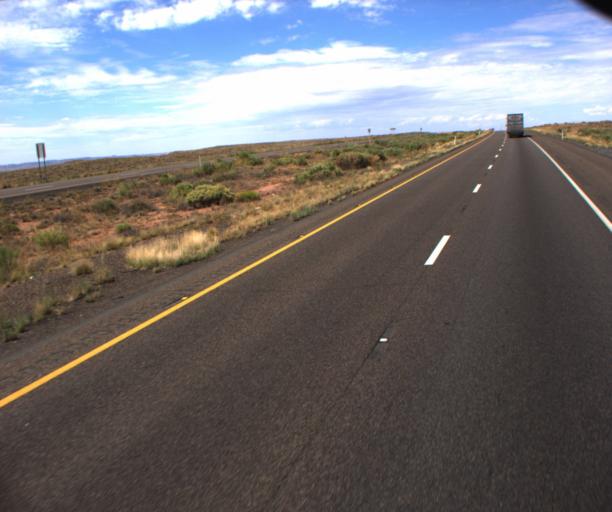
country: US
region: Arizona
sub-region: Navajo County
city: Holbrook
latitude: 35.0668
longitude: -109.7675
